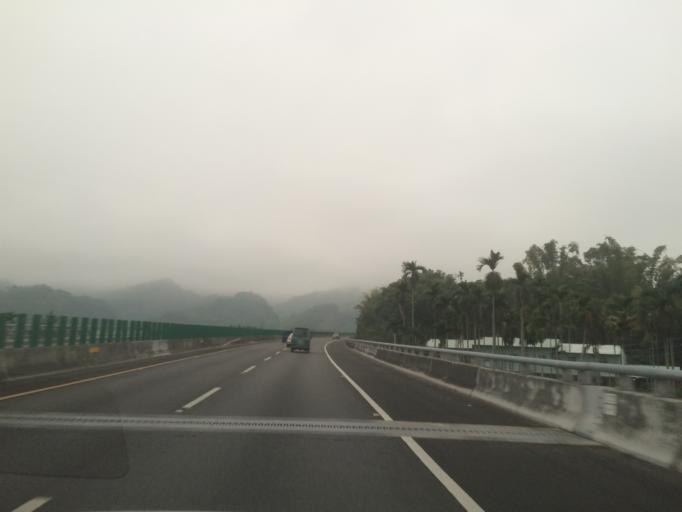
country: TW
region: Taiwan
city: Zhongxing New Village
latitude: 23.9860
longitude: 120.7789
